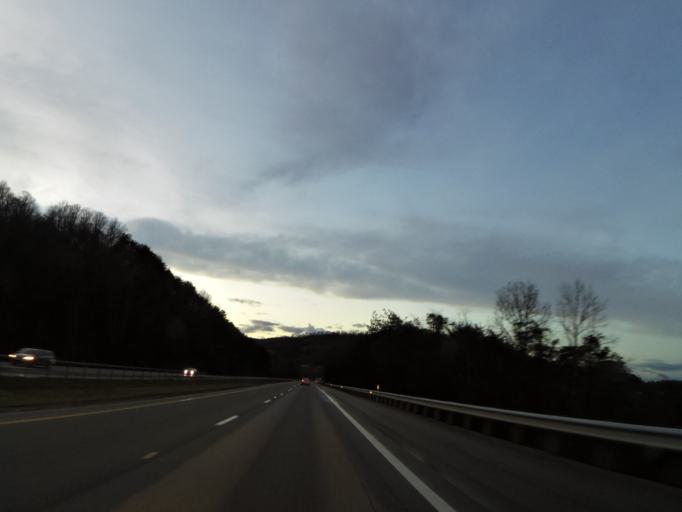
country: US
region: Kentucky
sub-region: Whitley County
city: Williamsburg
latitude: 36.6850
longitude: -84.1373
